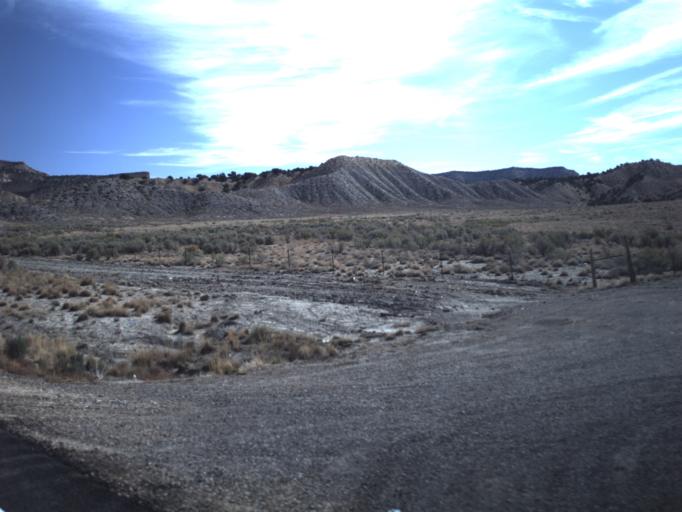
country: US
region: Utah
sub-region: Garfield County
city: Panguitch
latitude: 37.5990
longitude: -111.9734
